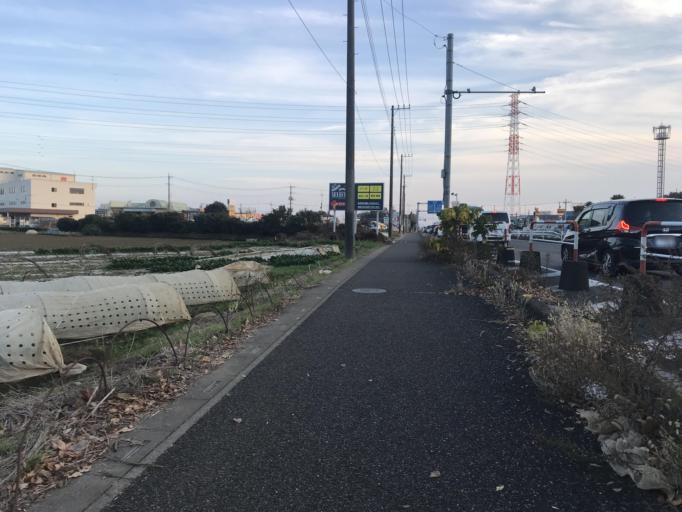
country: JP
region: Saitama
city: Tokorozawa
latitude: 35.8020
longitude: 139.4987
